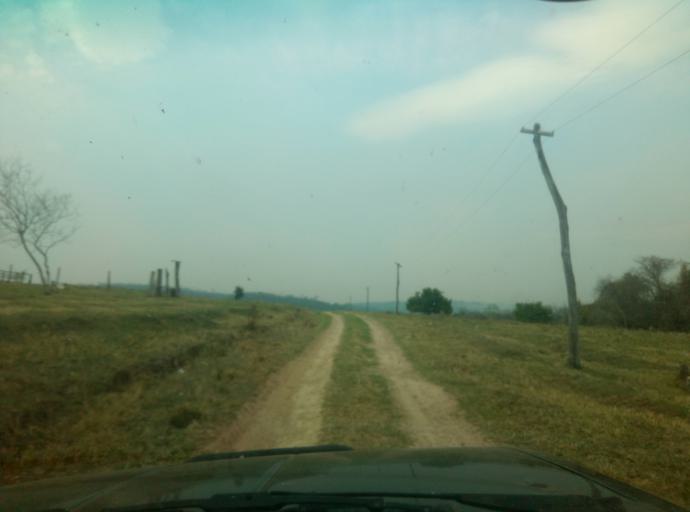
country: PY
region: Caaguazu
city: San Joaquin
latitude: -25.1036
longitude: -56.1261
